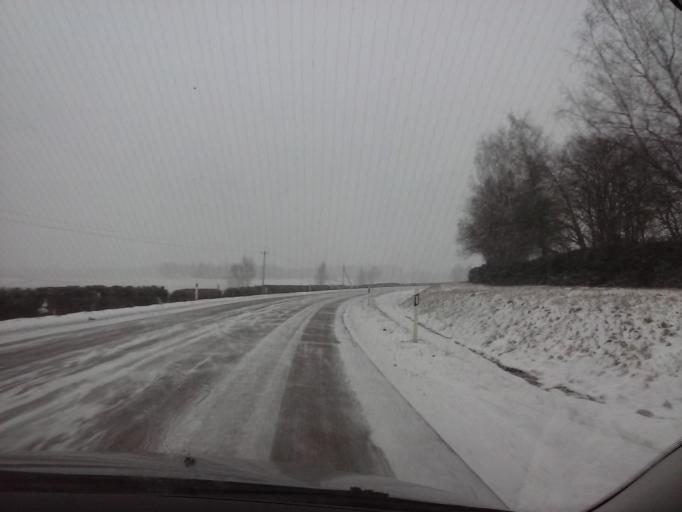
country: EE
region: Valgamaa
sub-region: Torva linn
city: Torva
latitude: 58.0467
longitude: 26.1926
